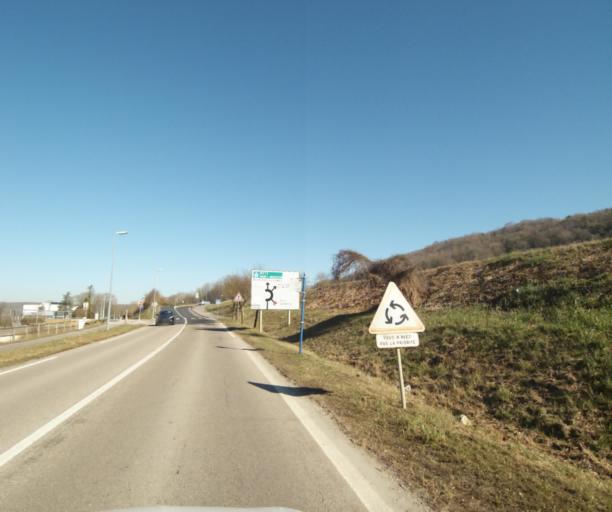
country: FR
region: Lorraine
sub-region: Departement de Meurthe-et-Moselle
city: Malzeville
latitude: 48.7300
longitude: 6.1826
